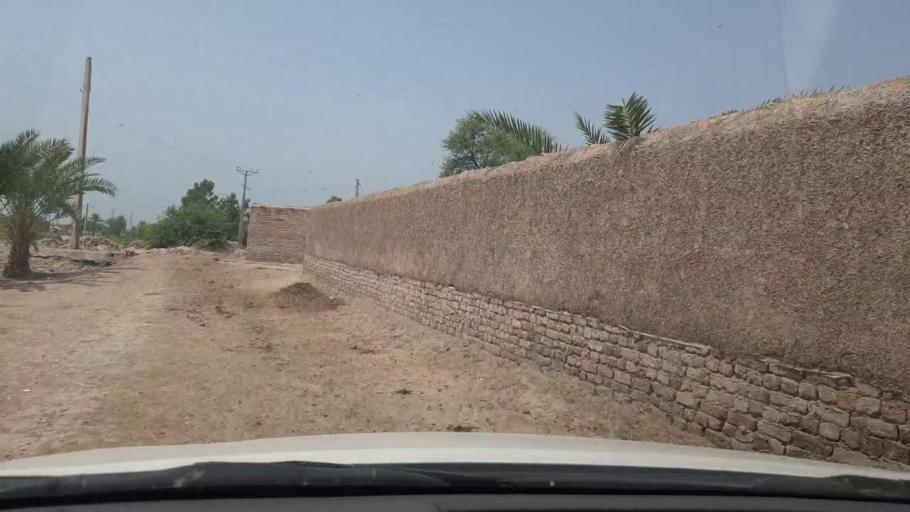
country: PK
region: Sindh
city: Shikarpur
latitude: 28.0080
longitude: 68.6460
